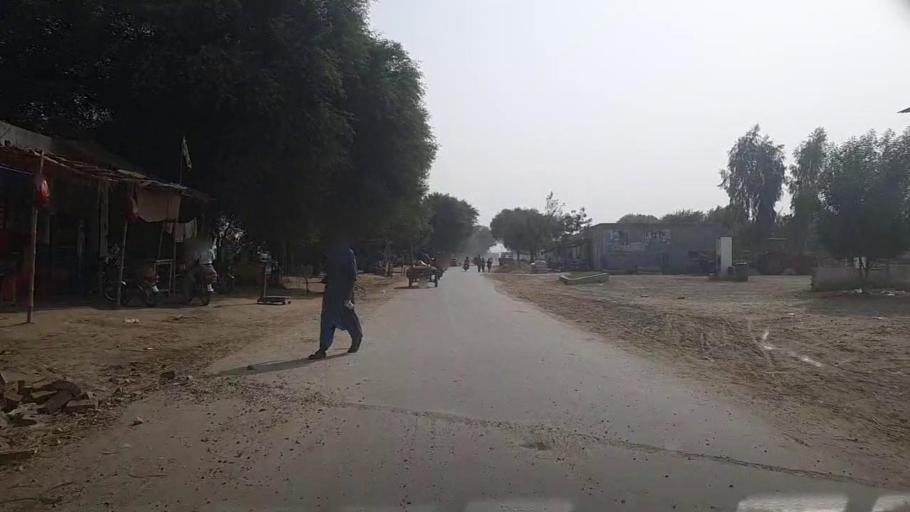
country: PK
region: Sindh
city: Kashmor
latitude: 28.4226
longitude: 69.5711
